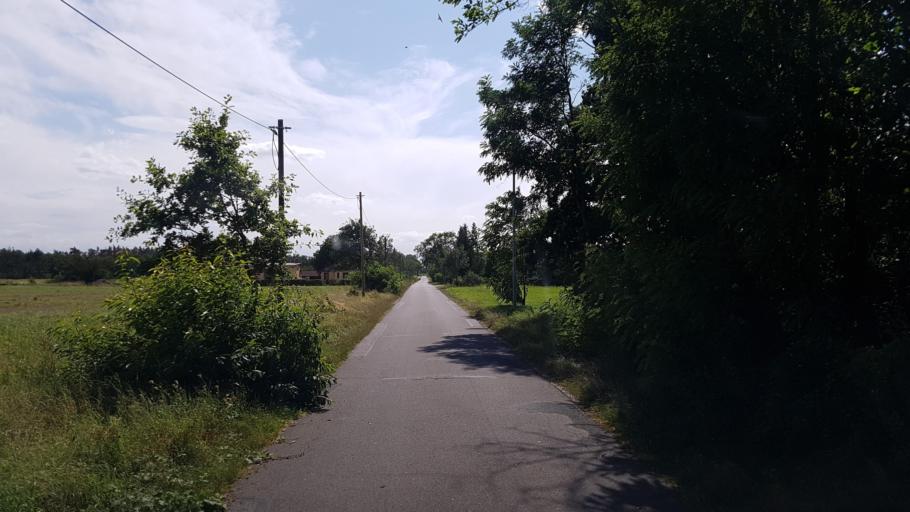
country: DE
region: Brandenburg
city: Muhlberg
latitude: 51.4494
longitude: 13.2949
